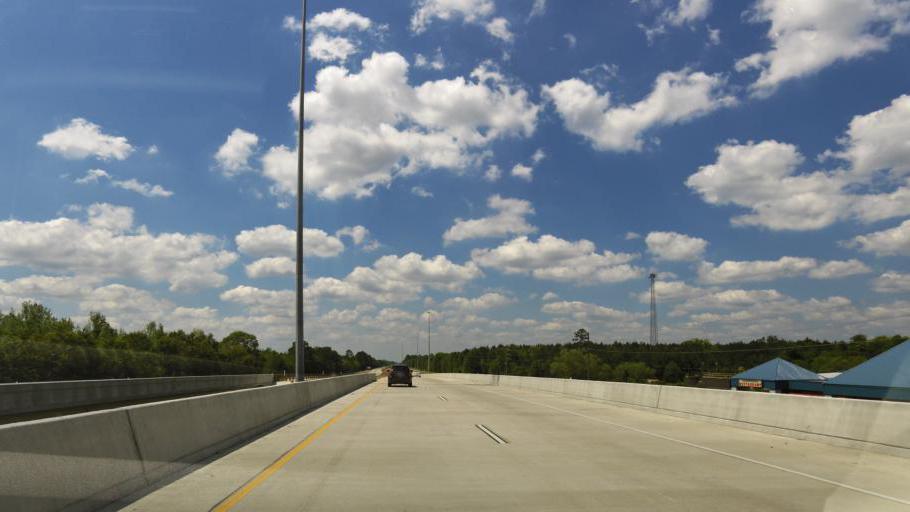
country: US
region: Texas
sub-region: San Jacinto County
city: Shepherd
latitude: 30.4452
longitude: -95.0297
